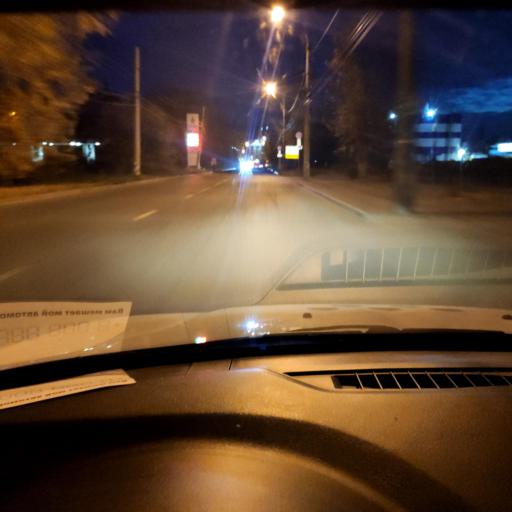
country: RU
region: Samara
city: Tol'yatti
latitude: 53.5157
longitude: 49.4560
